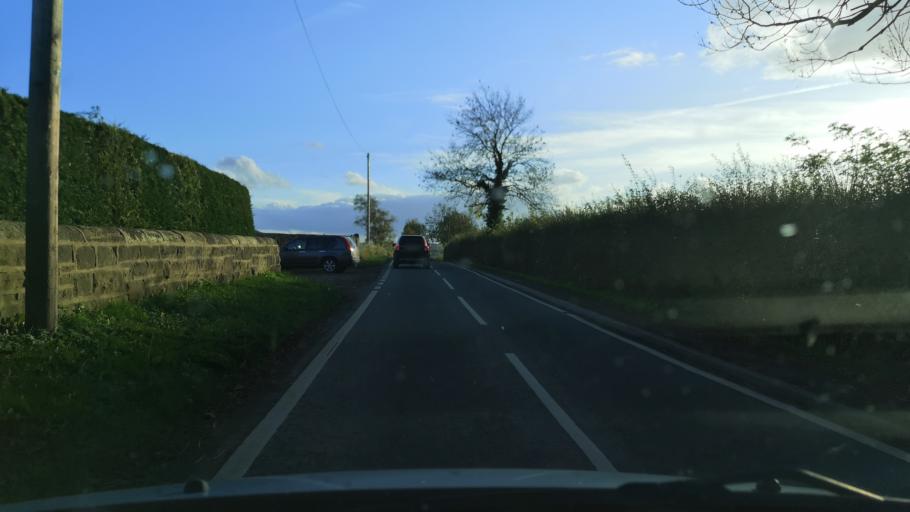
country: GB
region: England
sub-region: City and Borough of Wakefield
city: Low Ackworth
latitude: 53.6564
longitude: -1.3141
